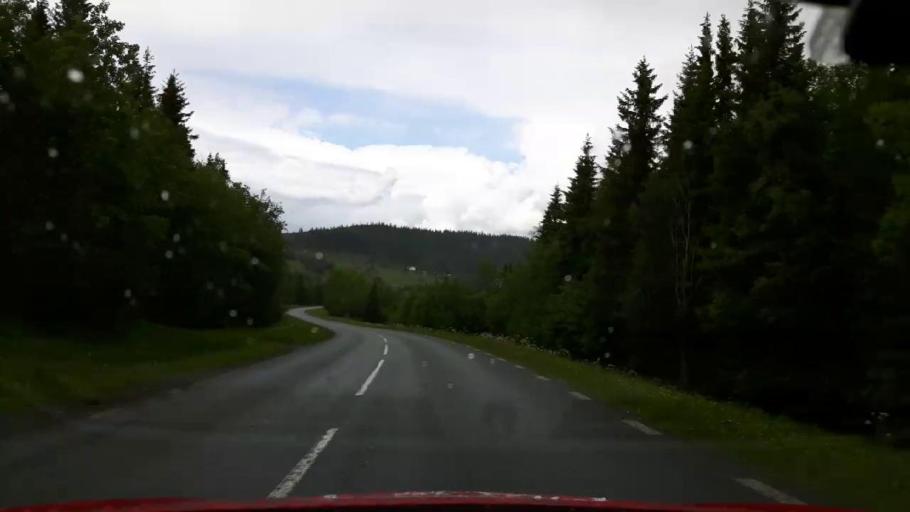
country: SE
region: Jaemtland
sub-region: Krokoms Kommun
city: Krokom
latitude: 63.4762
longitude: 14.1928
